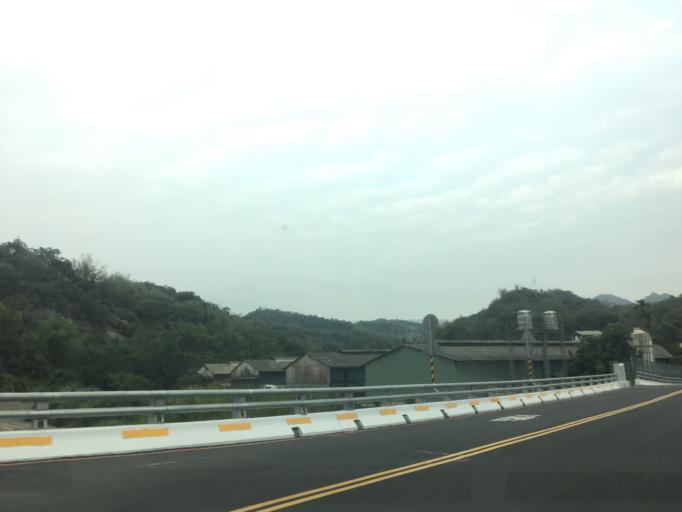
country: TW
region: Taiwan
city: Zhongxing New Village
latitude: 24.0359
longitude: 120.7339
